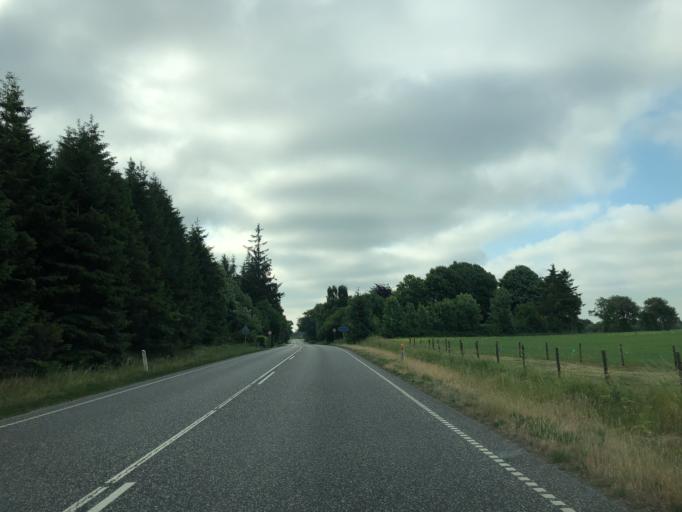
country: DK
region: South Denmark
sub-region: Vejle Kommune
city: Jelling
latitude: 55.7415
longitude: 9.3395
